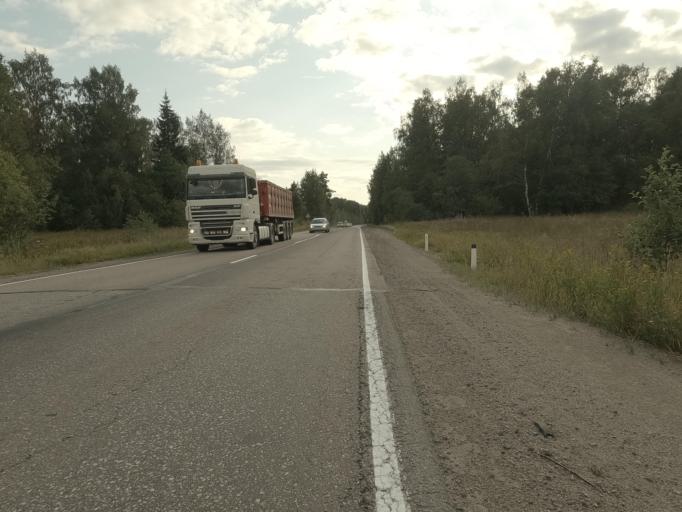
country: RU
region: Leningrad
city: Kamennogorsk
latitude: 60.8748
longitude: 29.0003
